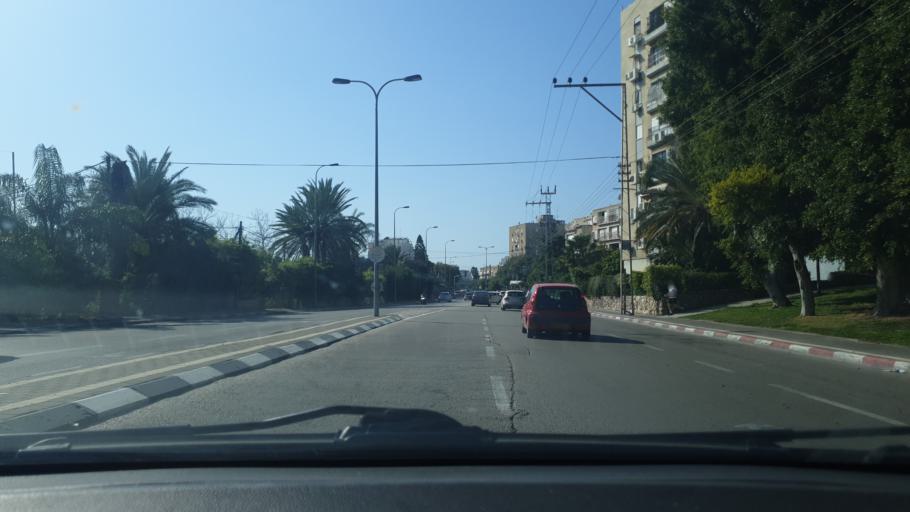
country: IL
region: Tel Aviv
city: Azor
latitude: 32.0446
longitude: 34.8129
